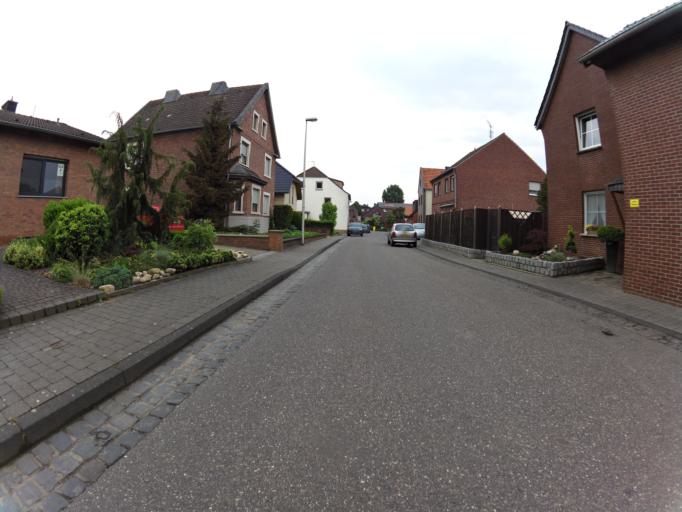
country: DE
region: North Rhine-Westphalia
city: Geilenkirchen
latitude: 50.9688
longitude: 6.1690
